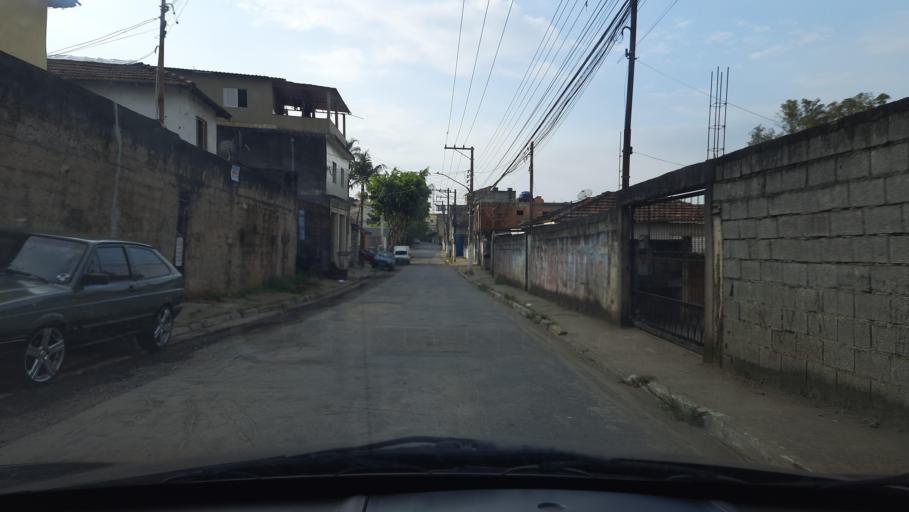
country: BR
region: Sao Paulo
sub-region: Caieiras
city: Caieiras
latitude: -23.4410
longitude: -46.7466
